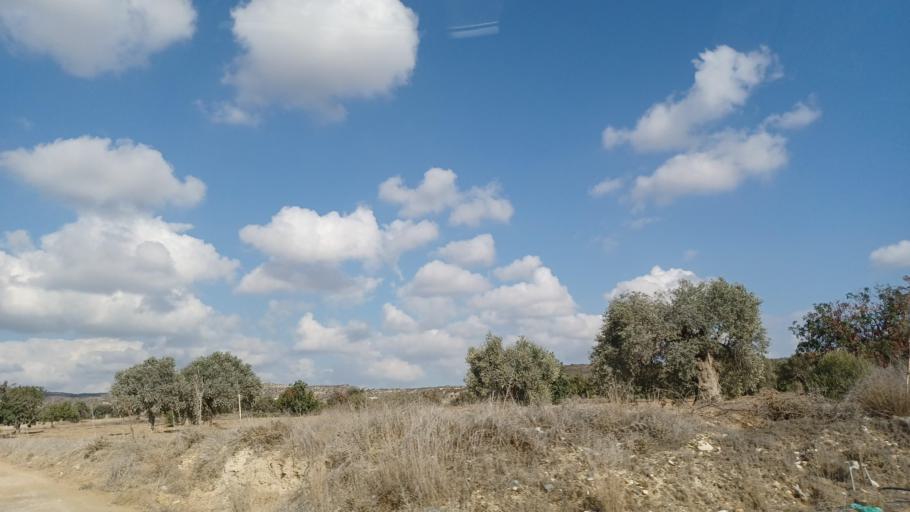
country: CY
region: Limassol
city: Pyrgos
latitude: 34.7261
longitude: 33.2477
